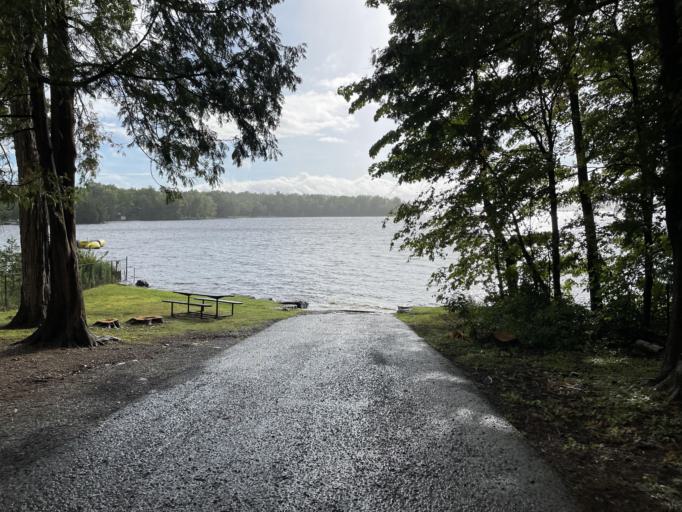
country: CA
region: Ontario
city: Quinte West
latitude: 44.4878
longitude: -77.8574
